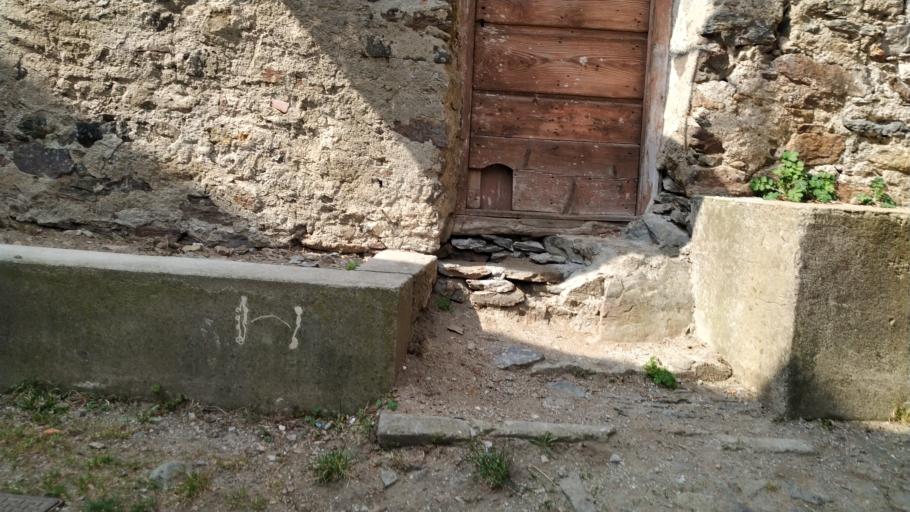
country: IT
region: Piedmont
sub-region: Provincia di Vercelli
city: Fobello
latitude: 45.8984
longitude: 8.1507
